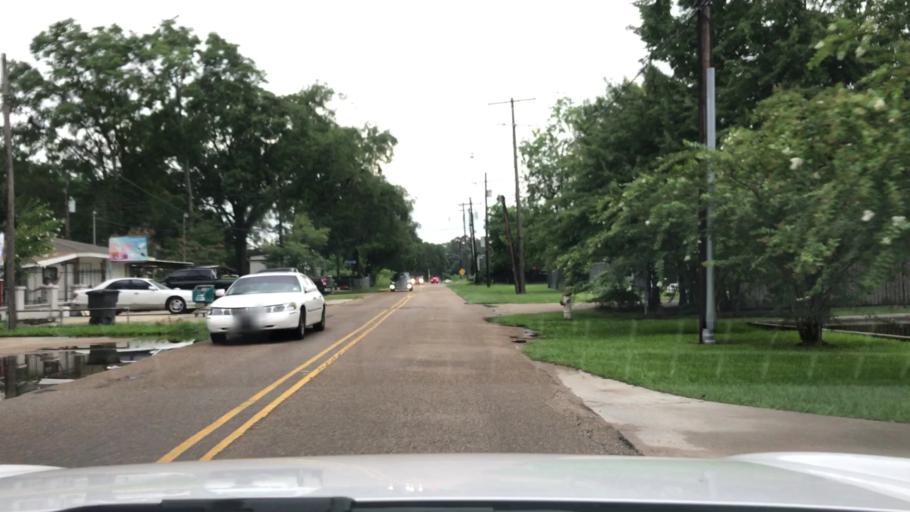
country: US
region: Louisiana
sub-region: East Baton Rouge Parish
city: Merrydale
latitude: 30.4807
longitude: -91.1176
